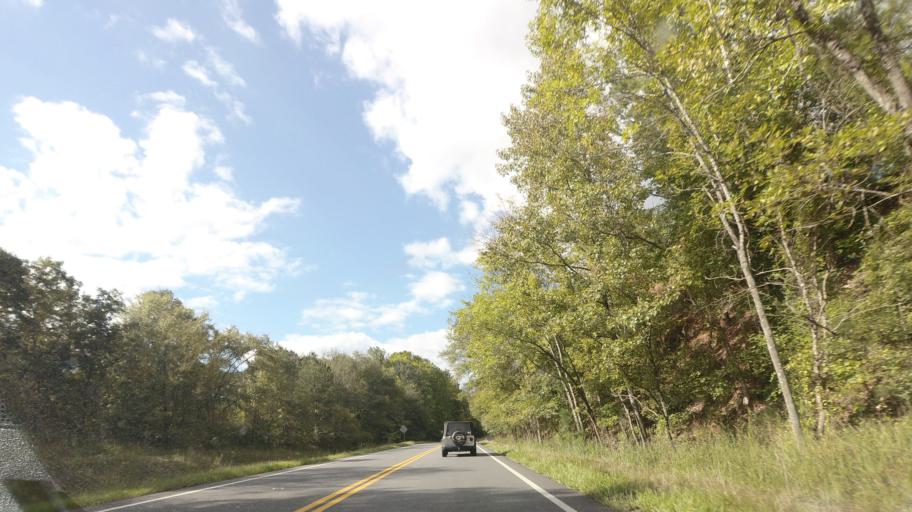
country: US
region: Georgia
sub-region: Monroe County
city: Forsyth
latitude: 33.0135
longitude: -83.7425
